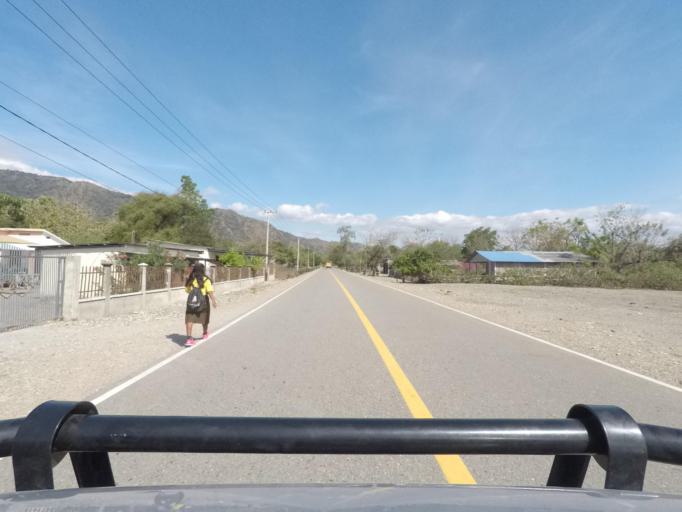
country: ID
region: East Nusa Tenggara
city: Atambua
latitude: -8.9151
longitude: 124.9940
